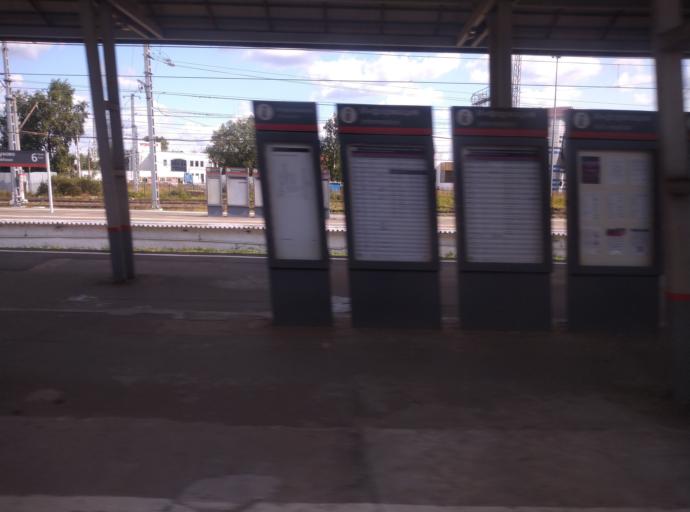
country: RU
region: St.-Petersburg
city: Obukhovo
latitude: 59.8483
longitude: 30.4549
